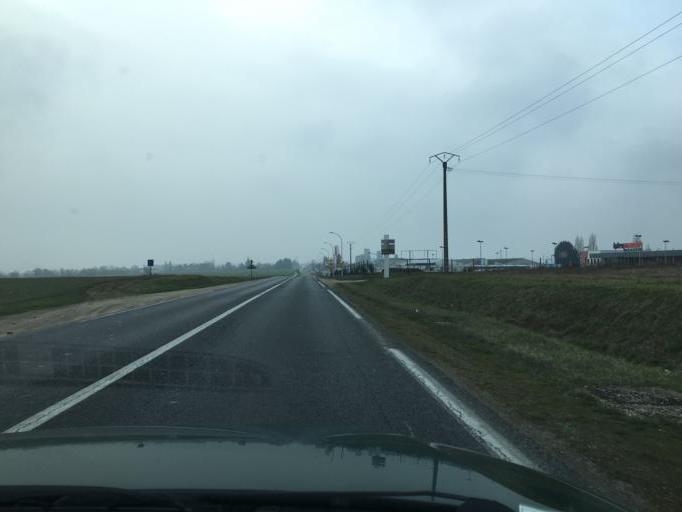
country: FR
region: Centre
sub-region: Departement du Loiret
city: Beaugency
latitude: 47.7925
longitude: 1.6470
